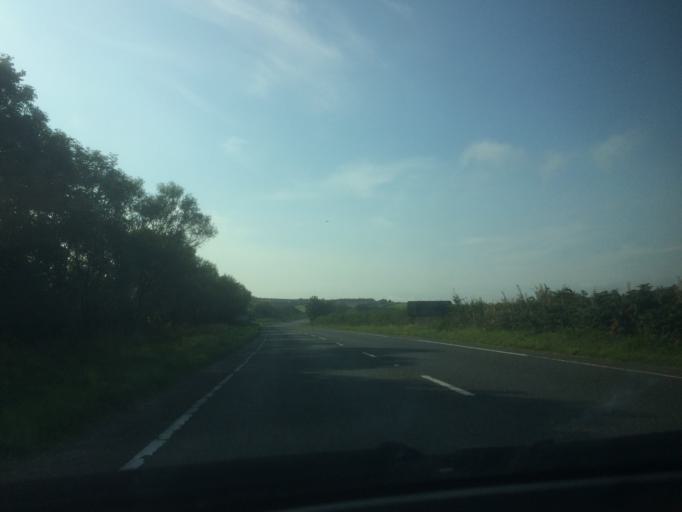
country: GB
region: England
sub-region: Cornwall
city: Callington
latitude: 50.4908
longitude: -4.2893
